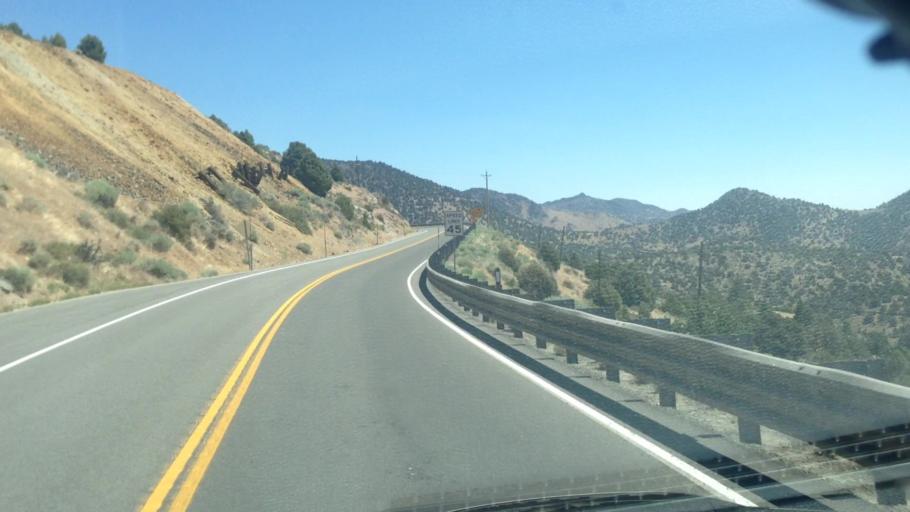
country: US
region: Nevada
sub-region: Storey County
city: Virginia City
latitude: 39.3188
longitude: -119.6455
